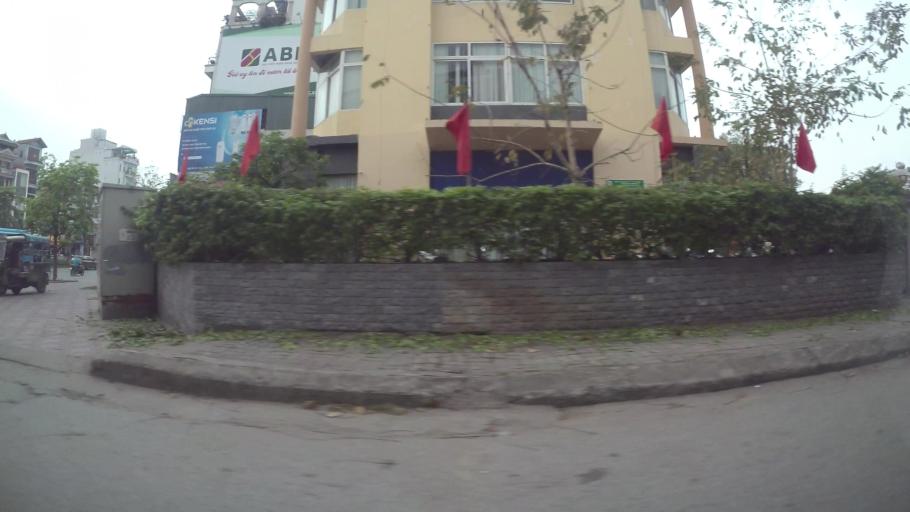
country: VN
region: Ha Noi
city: Hoan Kiem
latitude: 21.0602
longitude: 105.8934
